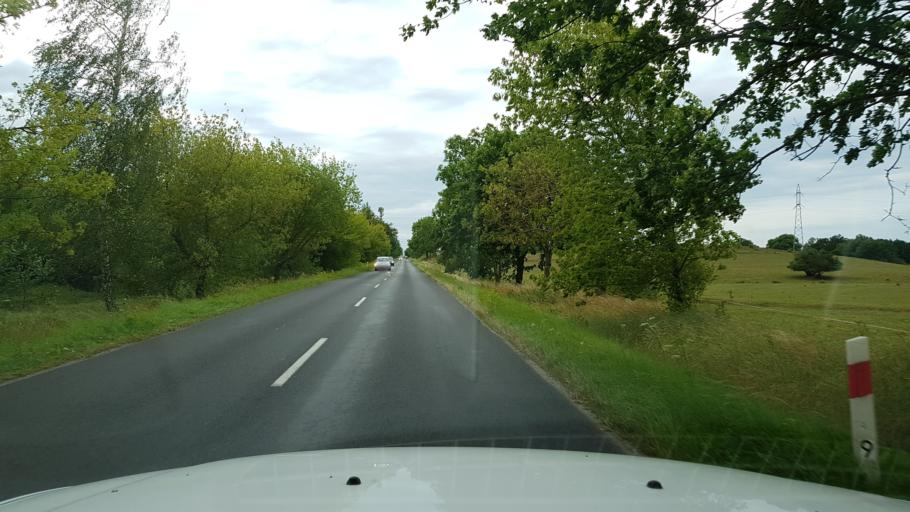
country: PL
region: West Pomeranian Voivodeship
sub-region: Powiat kolobrzeski
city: Kolobrzeg
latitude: 54.1489
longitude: 15.6399
